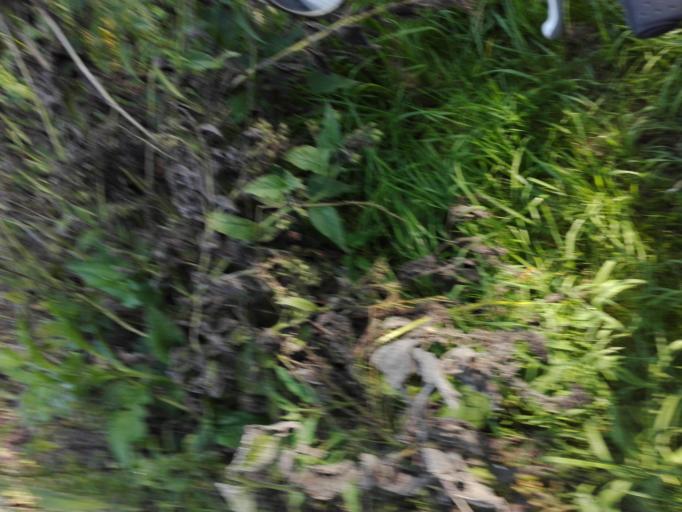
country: DK
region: Central Jutland
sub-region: Arhus Kommune
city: Lystrup
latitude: 56.2139
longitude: 10.1915
